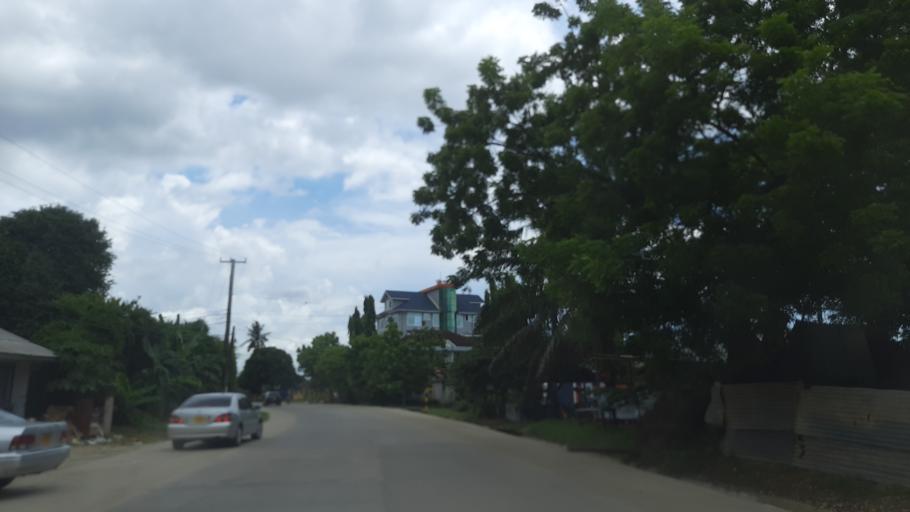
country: TZ
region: Dar es Salaam
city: Magomeni
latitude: -6.7799
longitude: 39.2385
